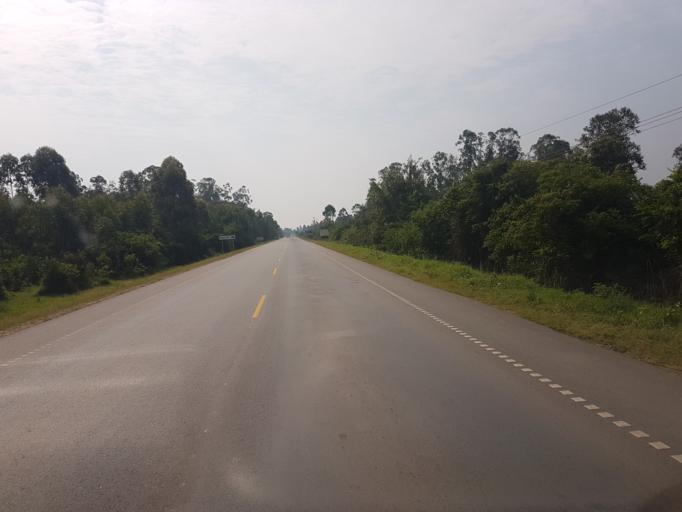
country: UG
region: Western Region
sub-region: Sheema District
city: Kibingo
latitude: -0.6350
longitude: 30.5257
